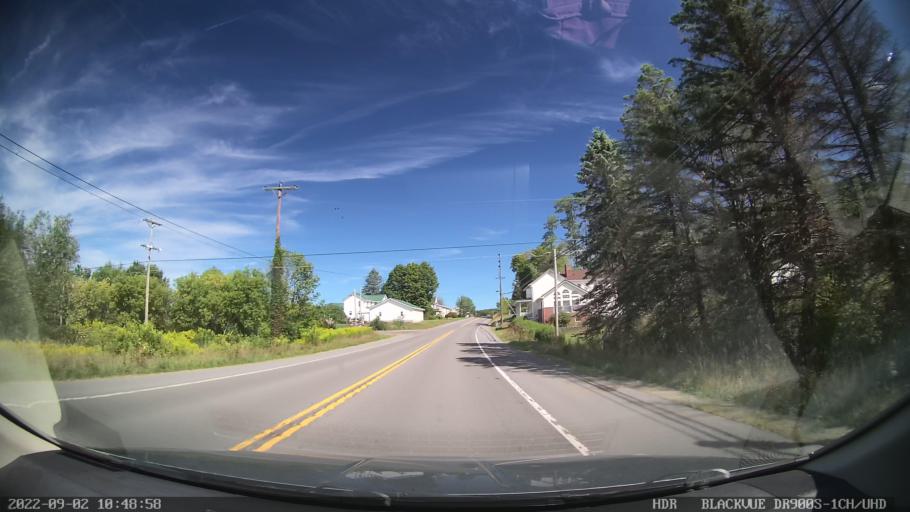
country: US
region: Pennsylvania
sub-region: Tioga County
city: Blossburg
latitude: 41.5941
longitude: -77.1101
